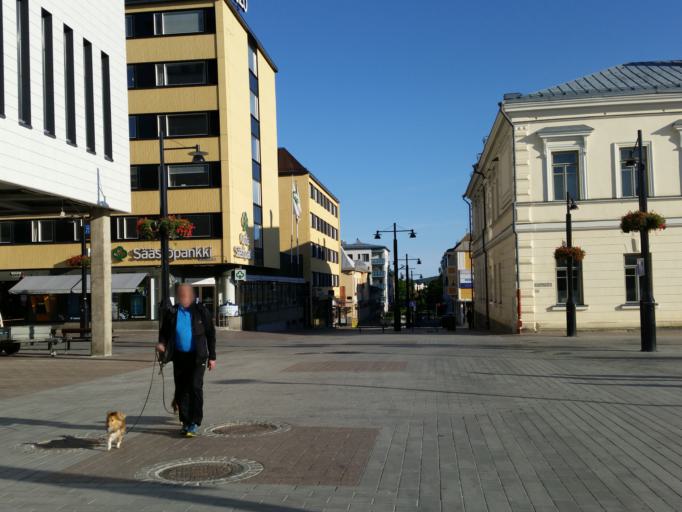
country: FI
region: Northern Savo
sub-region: Kuopio
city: Kuopio
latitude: 62.8920
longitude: 27.6798
